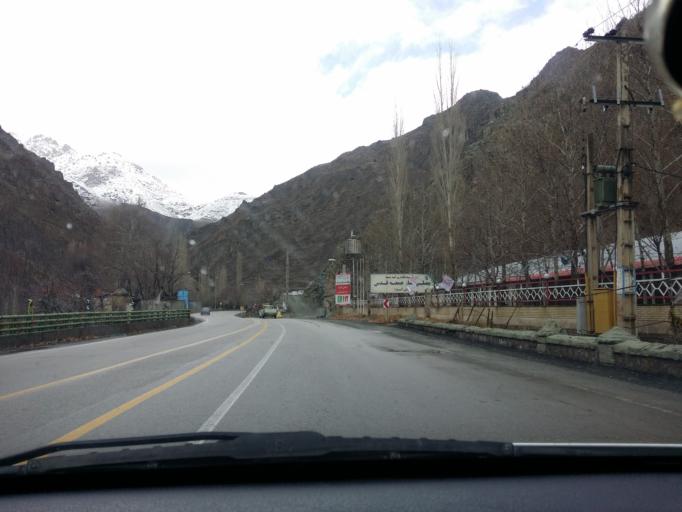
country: IR
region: Tehran
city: Tajrish
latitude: 36.0191
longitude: 51.3009
